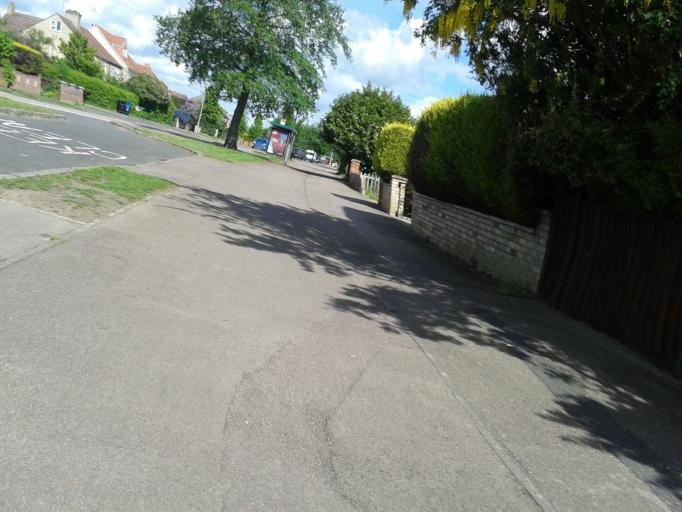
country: GB
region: England
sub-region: Cambridgeshire
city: Cambridge
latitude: 52.2243
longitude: 0.1489
